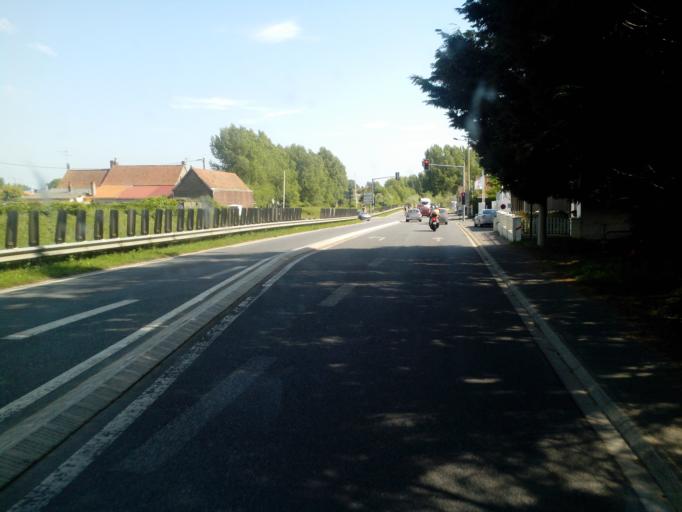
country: FR
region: Nord-Pas-de-Calais
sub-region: Departement du Pas-de-Calais
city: Verton
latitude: 50.3739
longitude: 1.6599
